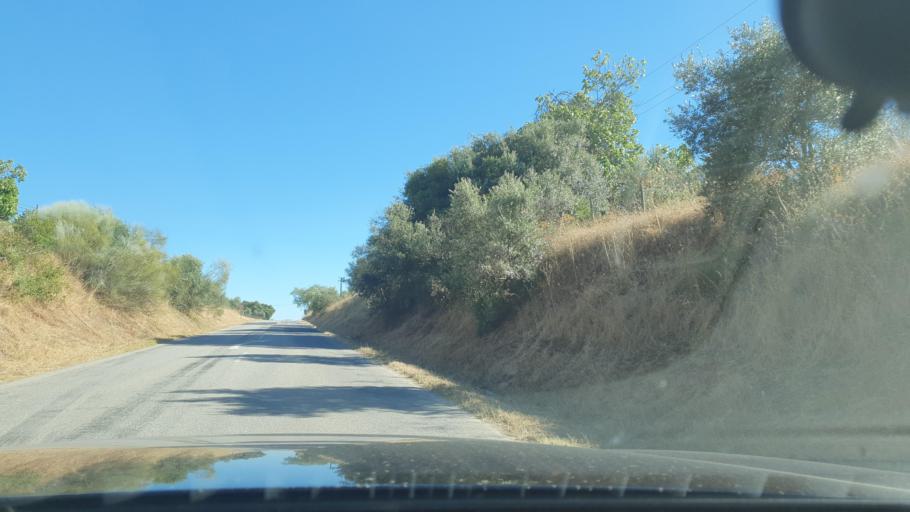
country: PT
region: Evora
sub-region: Alandroal
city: Alandroal
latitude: 38.7147
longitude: -7.4063
